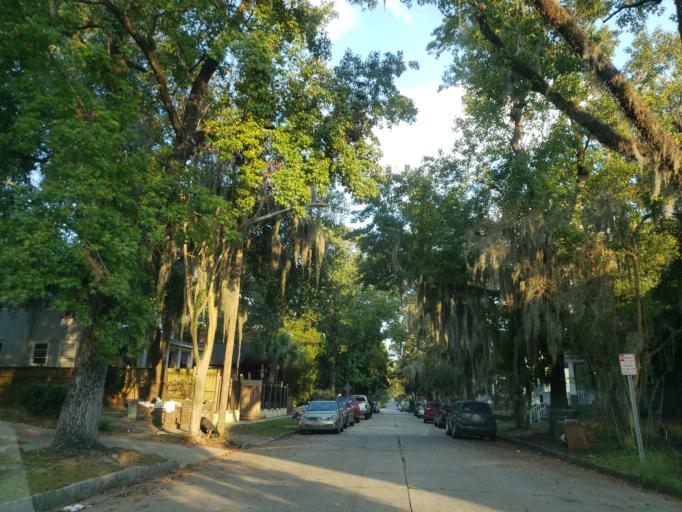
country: US
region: Georgia
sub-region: Chatham County
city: Savannah
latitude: 32.0553
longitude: -81.0806
